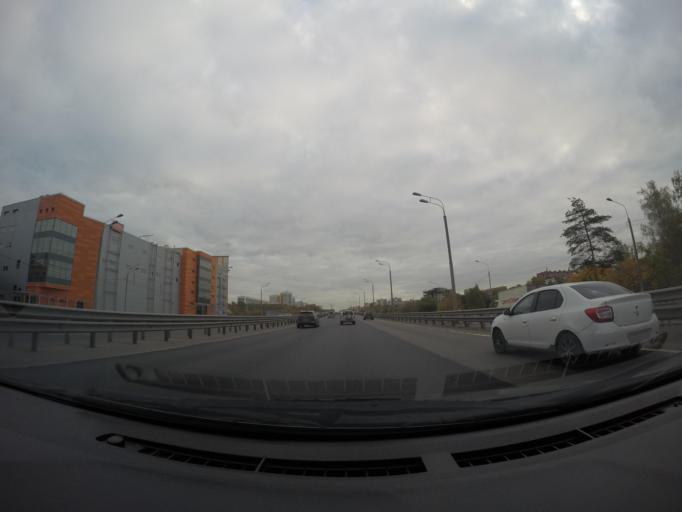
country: RU
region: Moskovskaya
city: Balashikha
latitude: 55.7948
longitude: 37.9492
